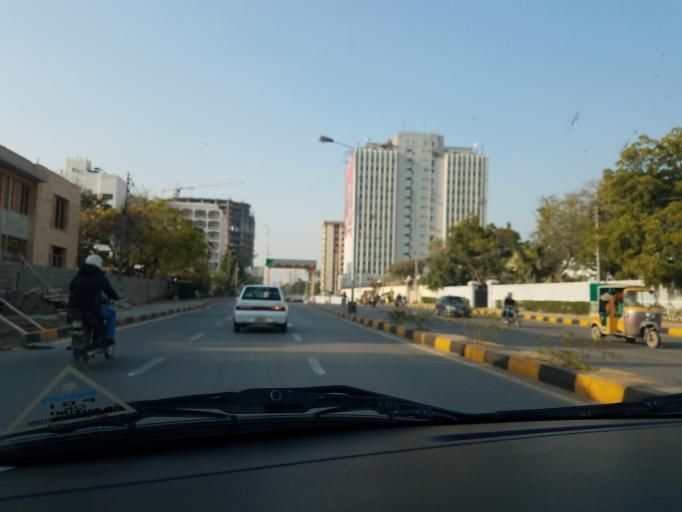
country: PK
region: Sindh
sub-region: Karachi District
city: Karachi
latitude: 24.8505
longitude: 67.0352
